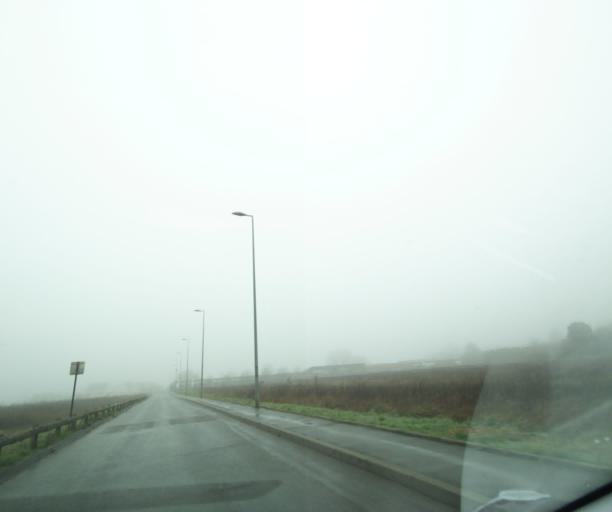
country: FR
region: Ile-de-France
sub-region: Departement de Seine-et-Marne
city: Longperrier
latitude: 49.0486
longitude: 2.6621
